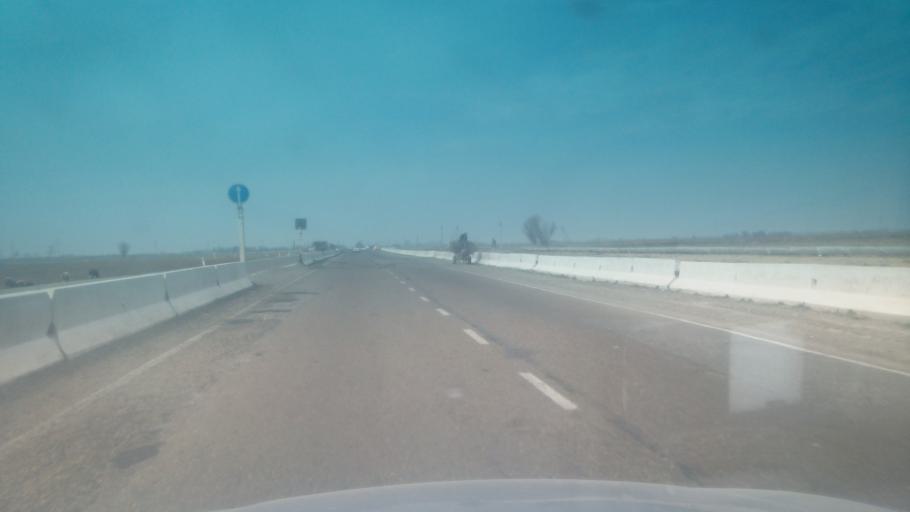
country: KZ
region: Ongtustik Qazaqstan
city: Myrzakent
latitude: 40.5186
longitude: 68.4723
